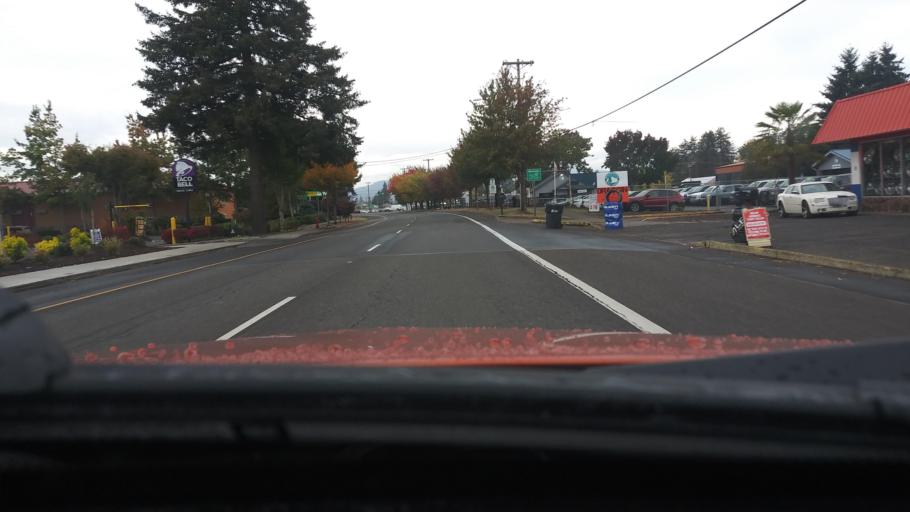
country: US
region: Oregon
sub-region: Washington County
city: Cornelius
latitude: 45.5210
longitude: -123.0702
